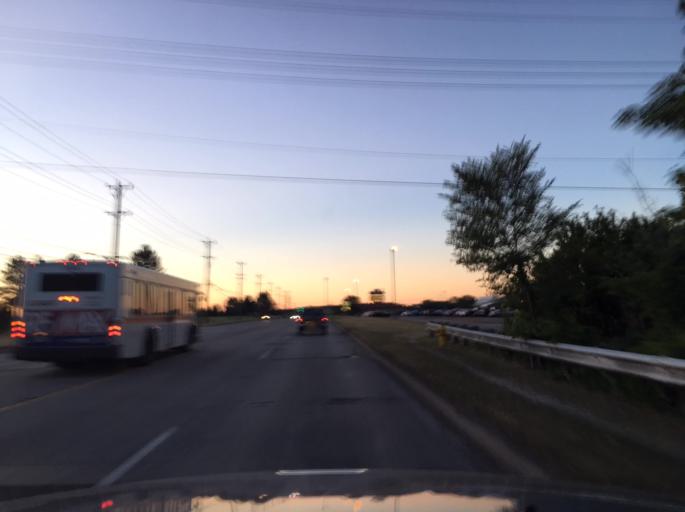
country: US
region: Michigan
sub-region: Macomb County
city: Clinton
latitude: 42.6238
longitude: -82.9532
